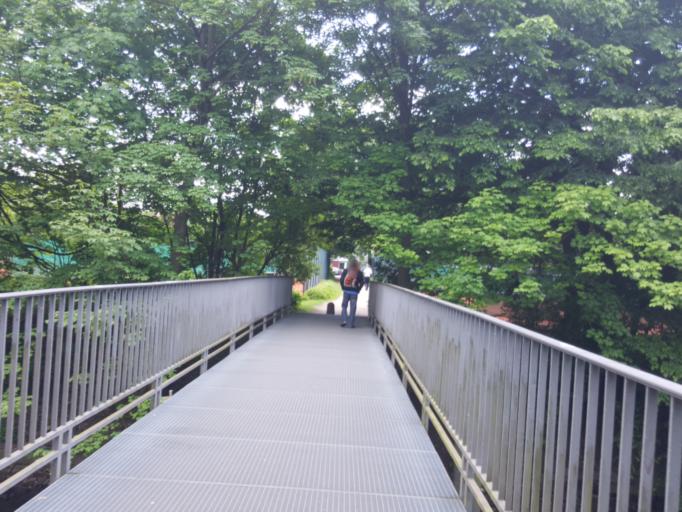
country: DE
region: Hamburg
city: Hammerbrook
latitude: 53.5493
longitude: 10.0301
